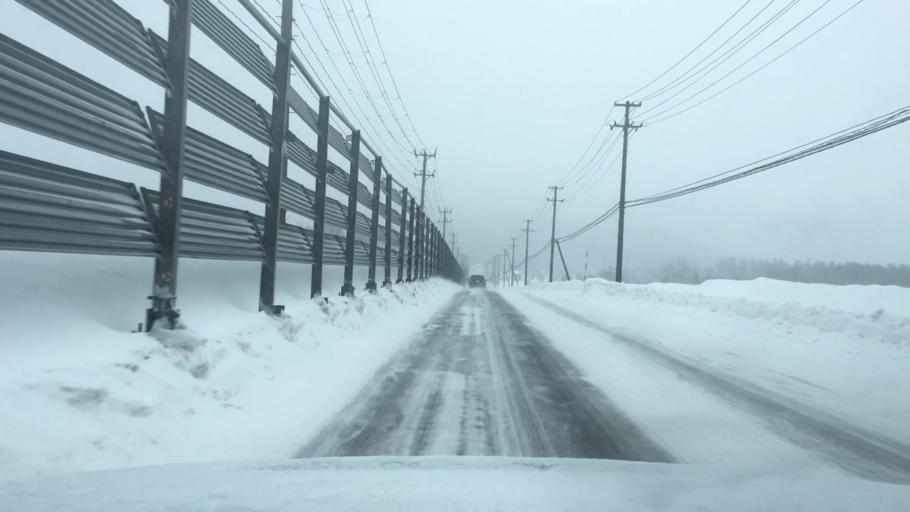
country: JP
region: Akita
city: Hanawa
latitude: 40.0126
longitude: 140.9827
